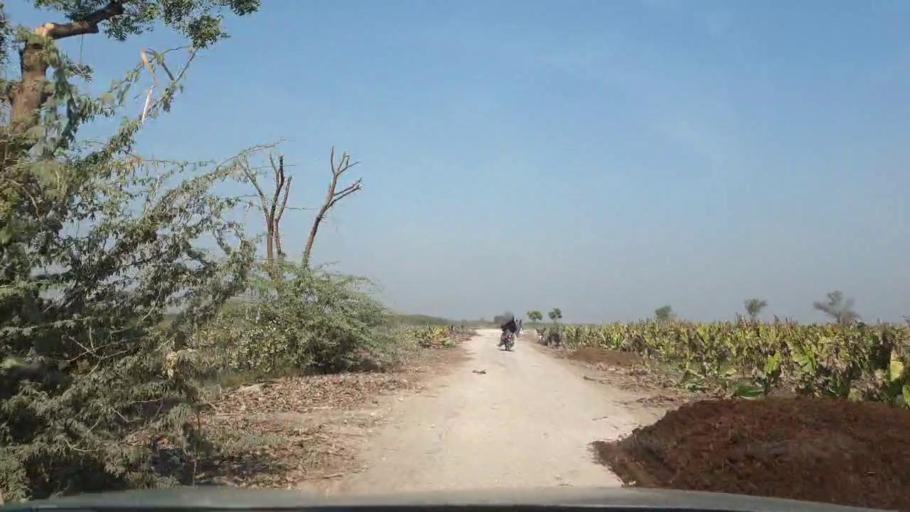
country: PK
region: Sindh
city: Tando Adam
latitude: 25.6303
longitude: 68.7384
